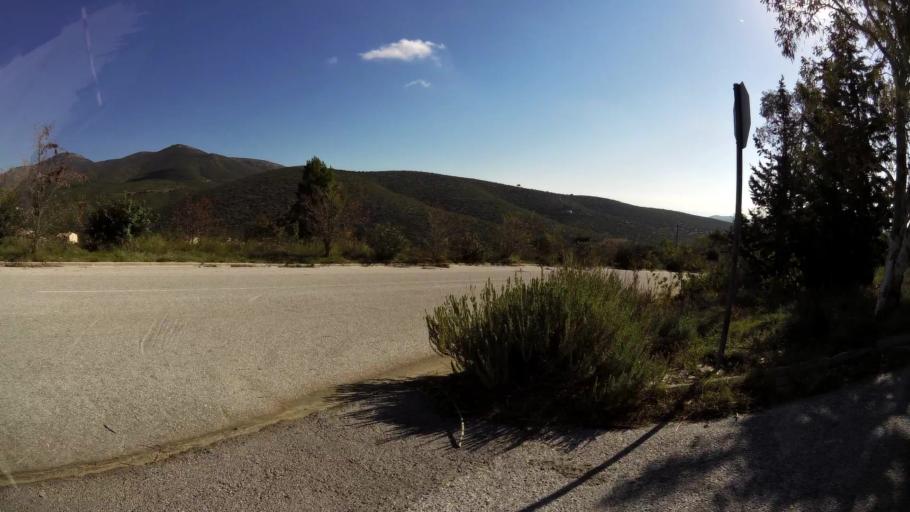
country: GR
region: Attica
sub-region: Nomarchia Anatolikis Attikis
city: Dhrafi
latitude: 38.0336
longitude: 23.9020
